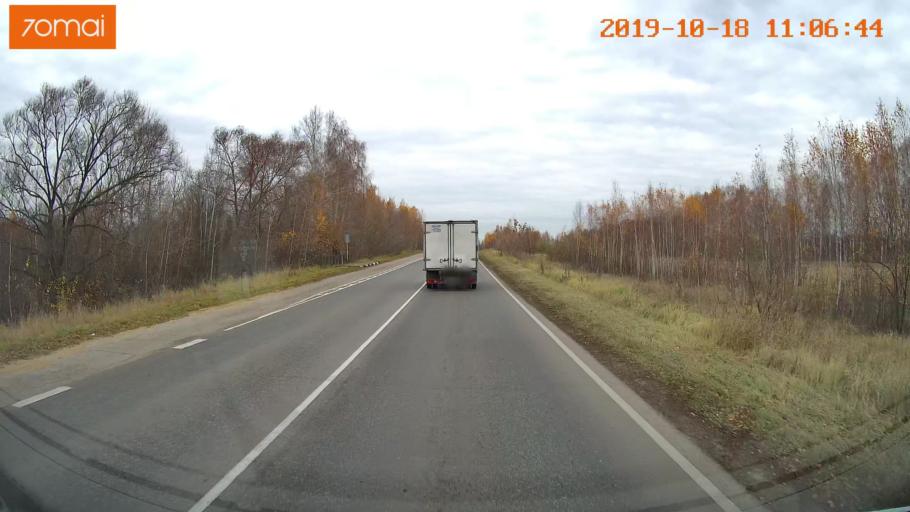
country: RU
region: Tula
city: Kimovsk
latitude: 53.9209
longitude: 38.5348
